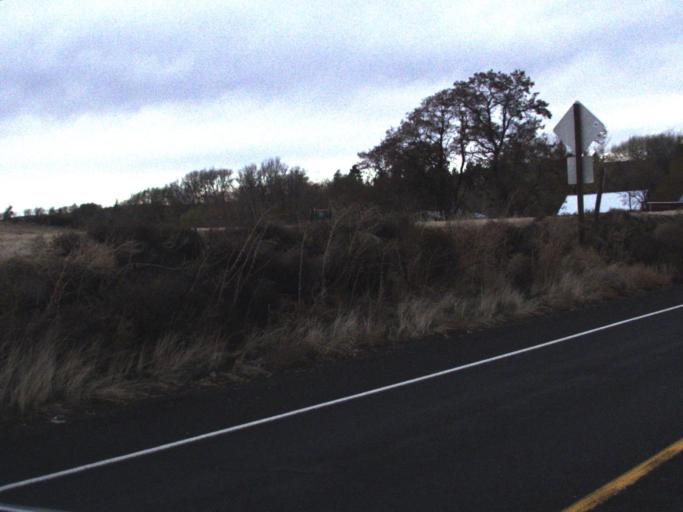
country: US
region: Washington
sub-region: Walla Walla County
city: Waitsburg
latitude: 46.2606
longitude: -118.1532
